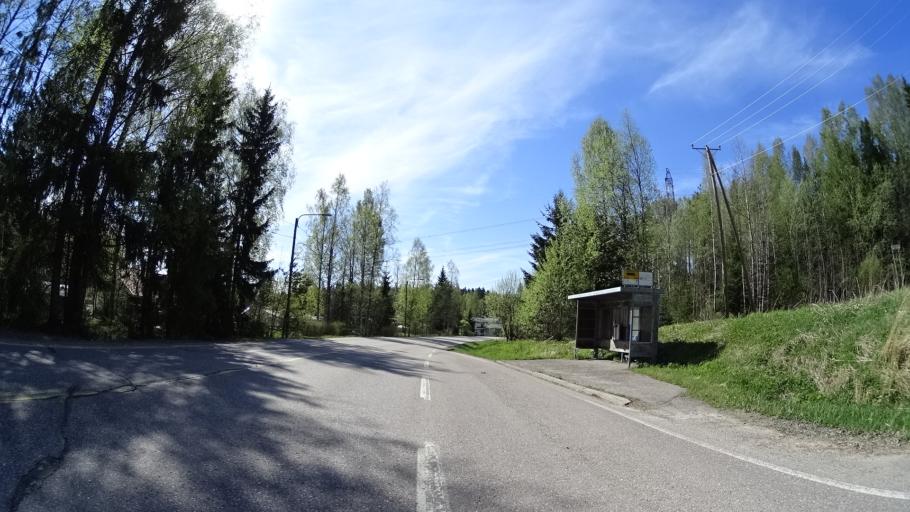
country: FI
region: Uusimaa
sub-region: Helsinki
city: Nurmijaervi
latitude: 60.3854
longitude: 24.8372
